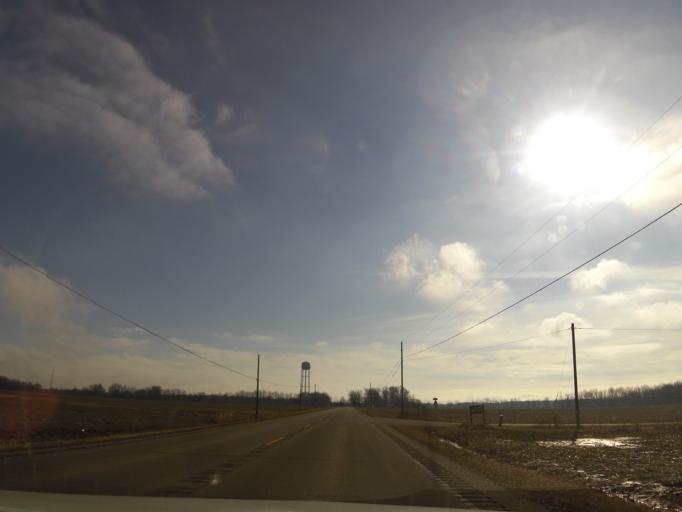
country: US
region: Indiana
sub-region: Jennings County
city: North Vernon
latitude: 38.8978
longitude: -85.5323
